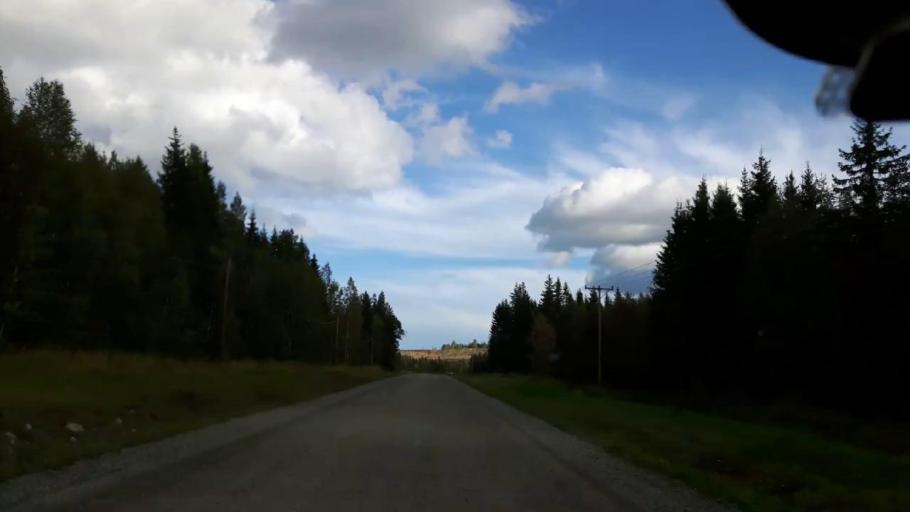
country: SE
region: Jaemtland
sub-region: Stroemsunds Kommun
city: Stroemsund
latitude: 63.3018
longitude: 15.5760
